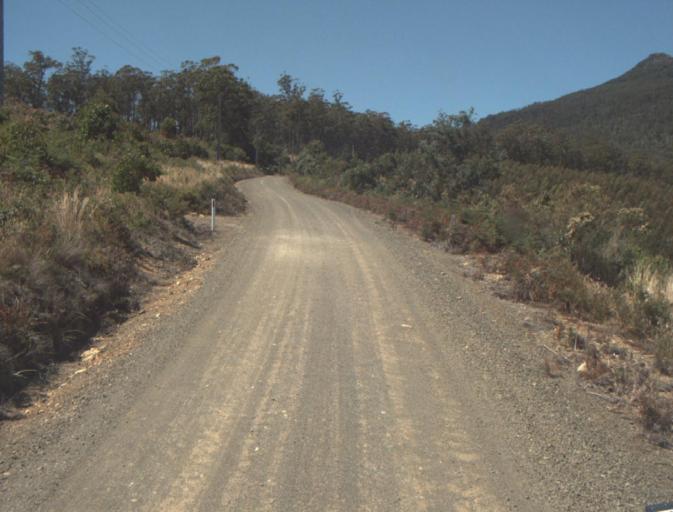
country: AU
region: Tasmania
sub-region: Launceston
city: Newstead
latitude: -41.3504
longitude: 147.3829
